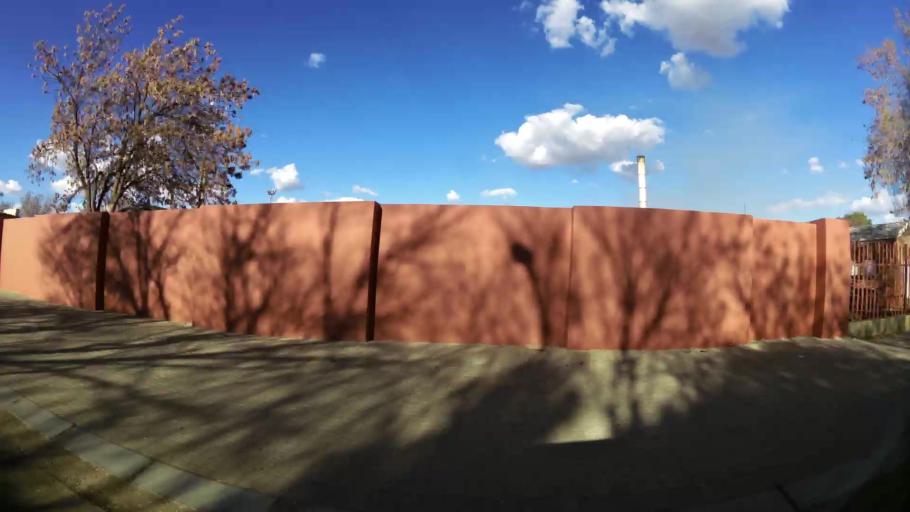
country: ZA
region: North-West
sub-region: Dr Kenneth Kaunda District Municipality
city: Klerksdorp
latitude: -26.8427
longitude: 26.6618
